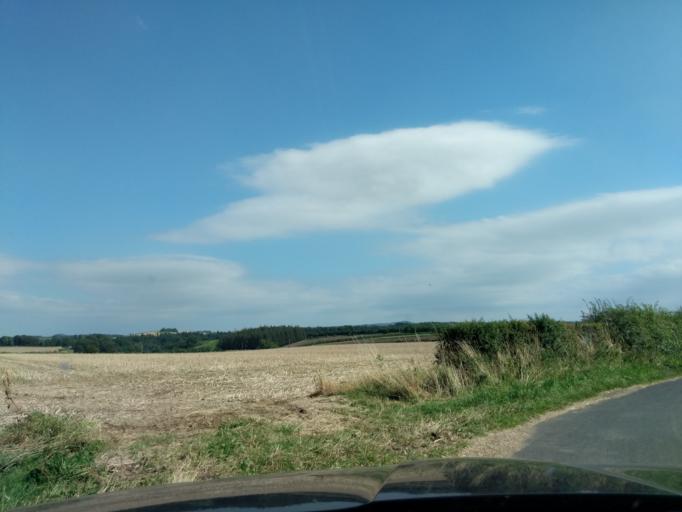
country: GB
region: Scotland
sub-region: The Scottish Borders
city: Coldstream
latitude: 55.6738
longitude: -2.1795
